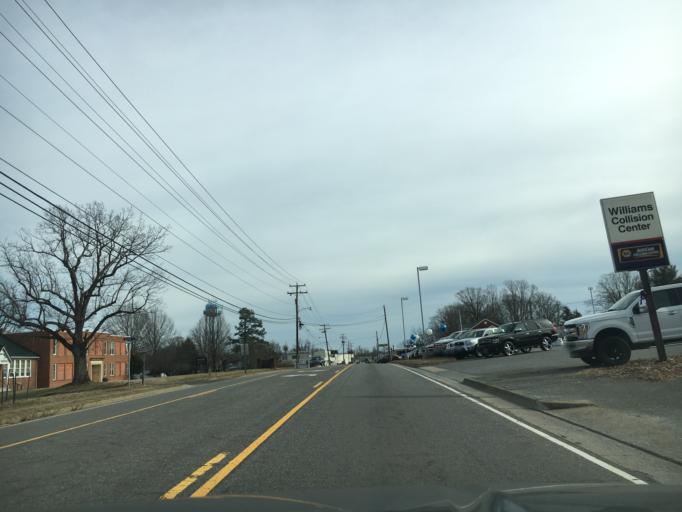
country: US
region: Virginia
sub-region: Appomattox County
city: Appomattox
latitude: 37.3607
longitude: -78.8304
